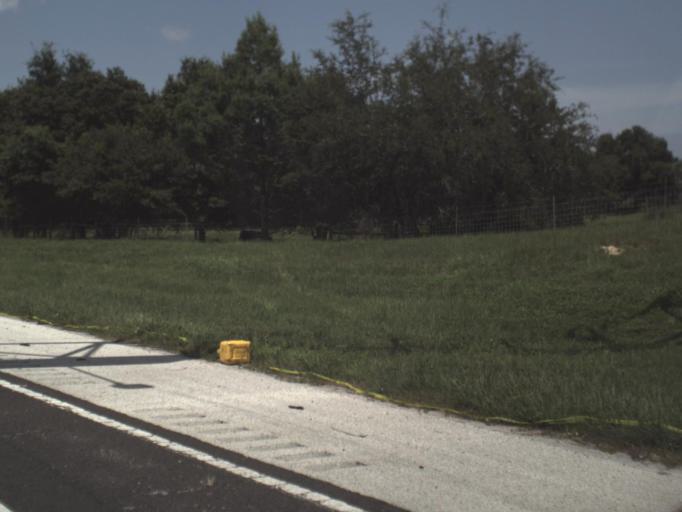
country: US
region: Florida
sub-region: Hillsborough County
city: Dover
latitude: 28.0273
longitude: -82.1727
